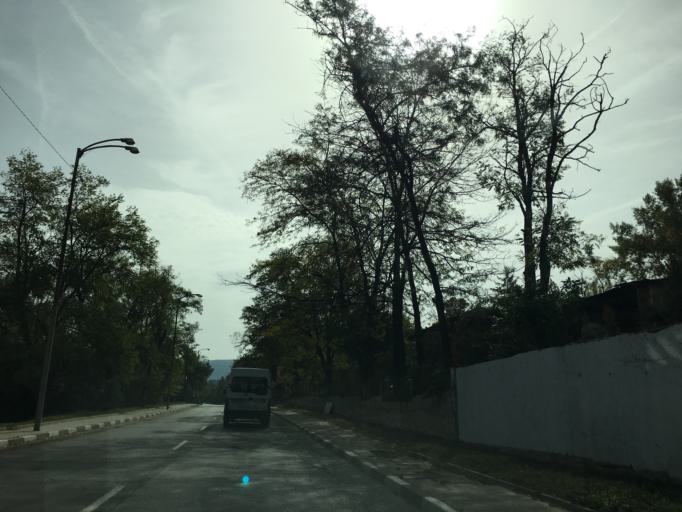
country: BG
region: Sofia-Capital
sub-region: Stolichna Obshtina
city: Sofia
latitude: 42.5888
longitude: 23.4194
